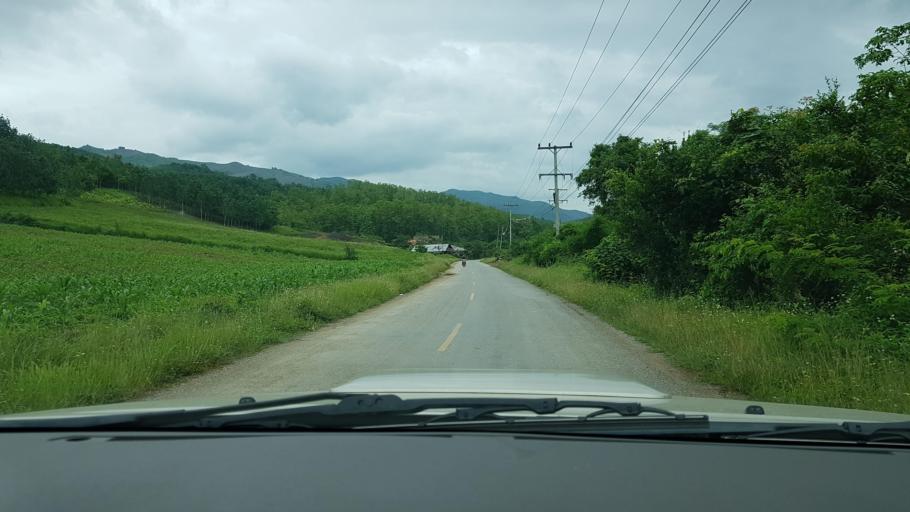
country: LA
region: Loungnamtha
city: Muang Nale
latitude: 20.2609
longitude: 101.5925
